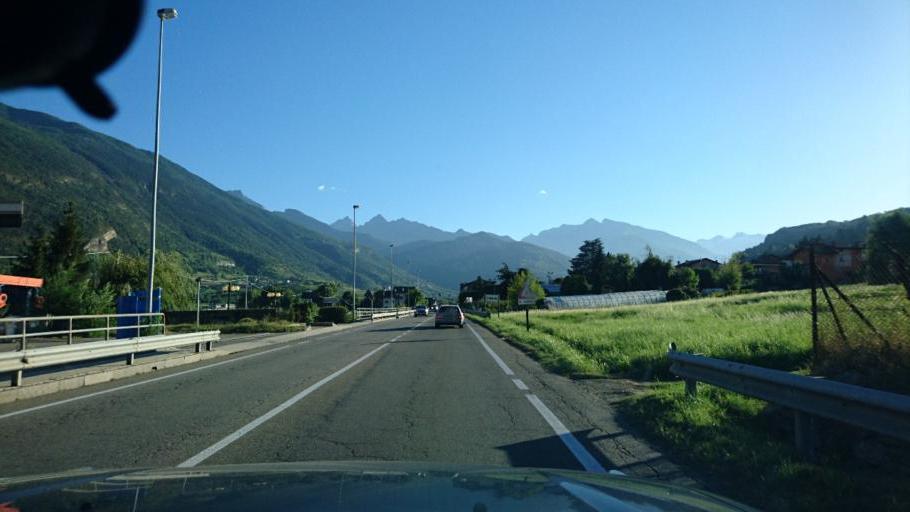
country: IT
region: Aosta Valley
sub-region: Valle d'Aosta
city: Saint Maurice
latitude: 45.7199
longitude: 7.2642
